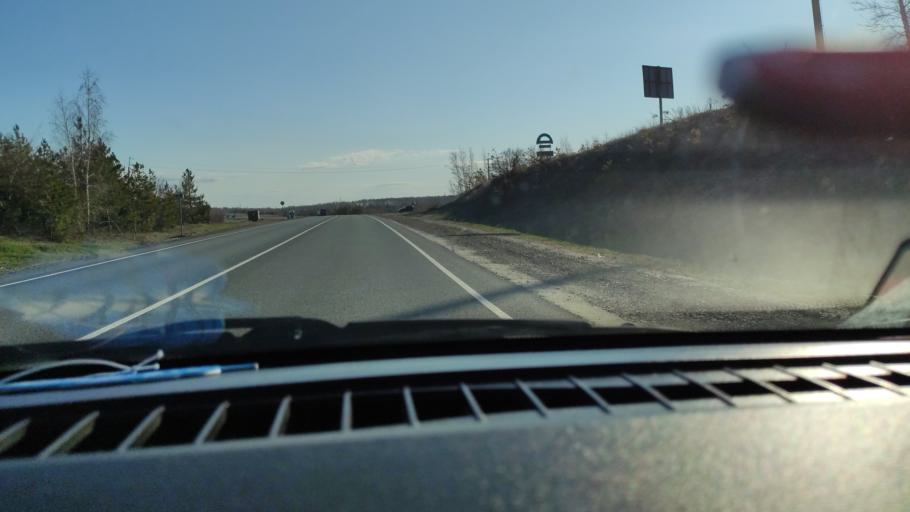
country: RU
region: Saratov
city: Khvalynsk
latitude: 52.5432
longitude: 48.0623
